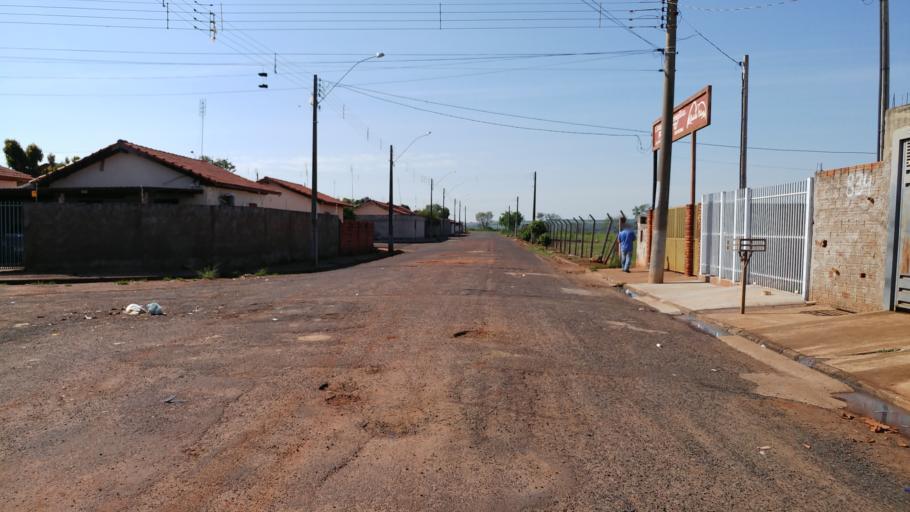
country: BR
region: Sao Paulo
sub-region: Paraguacu Paulista
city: Paraguacu Paulista
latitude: -22.4083
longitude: -50.5631
